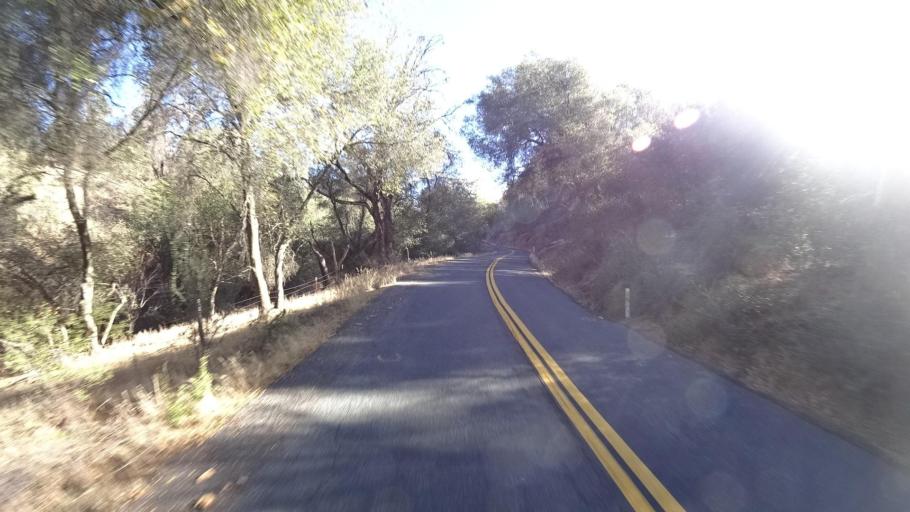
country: US
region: California
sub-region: Kern County
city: Alta Sierra
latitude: 35.7885
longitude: -118.7508
